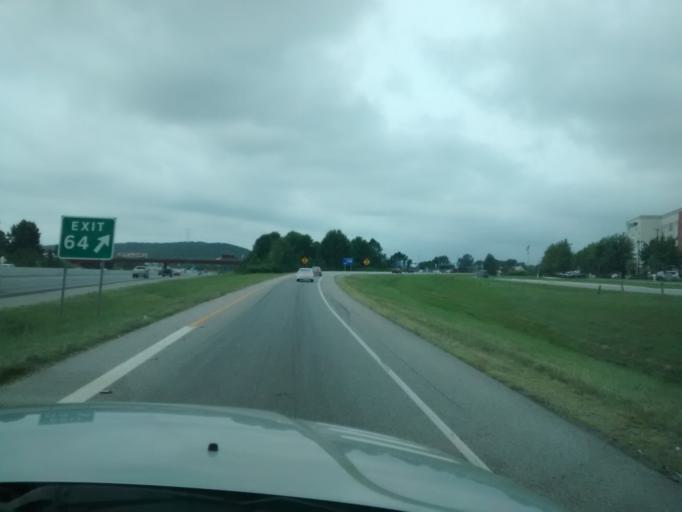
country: US
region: Arkansas
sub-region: Washington County
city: Fayetteville
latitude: 36.0814
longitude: -94.1993
